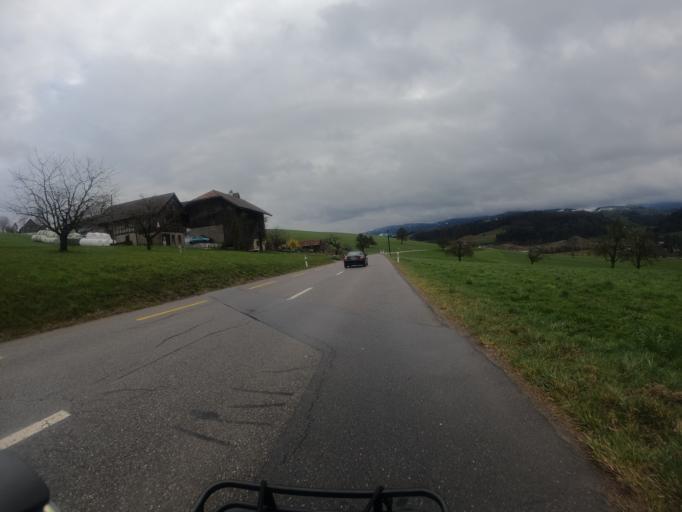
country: CH
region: Zurich
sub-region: Bezirk Affoltern
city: Hausen am Albis / Hausen (Dorf)
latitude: 47.2223
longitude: 8.5563
